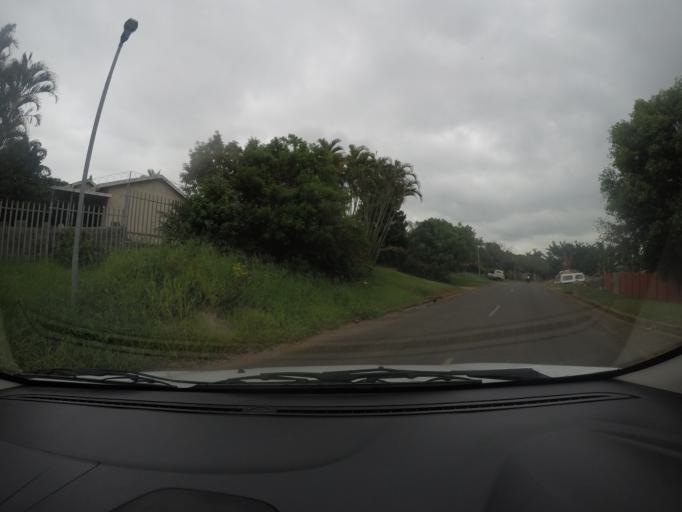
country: ZA
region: KwaZulu-Natal
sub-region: uThungulu District Municipality
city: Empangeni
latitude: -28.7656
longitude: 31.8892
